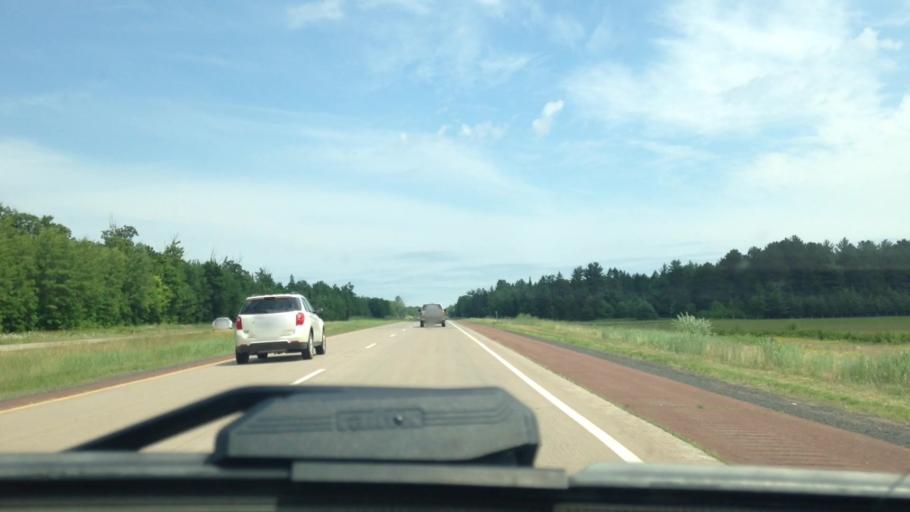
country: US
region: Wisconsin
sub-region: Douglas County
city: Lake Nebagamon
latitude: 46.3647
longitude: -91.8300
